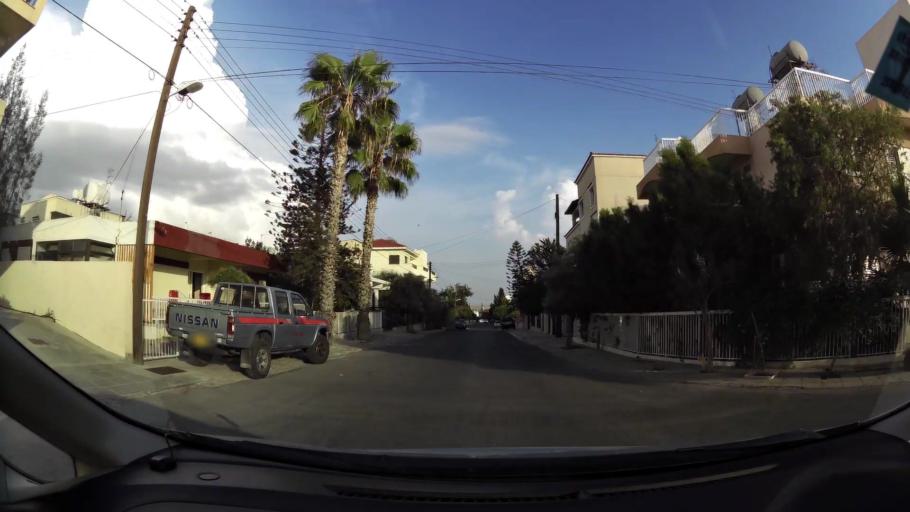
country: CY
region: Lefkosia
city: Nicosia
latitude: 35.1619
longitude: 33.3896
